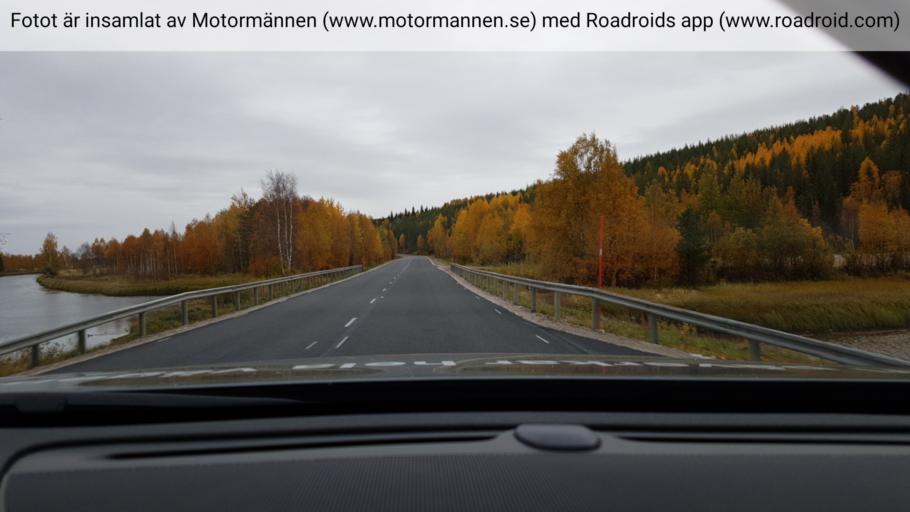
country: SE
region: Norrbotten
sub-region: Overkalix Kommun
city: OEverkalix
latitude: 66.4586
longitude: 22.7906
